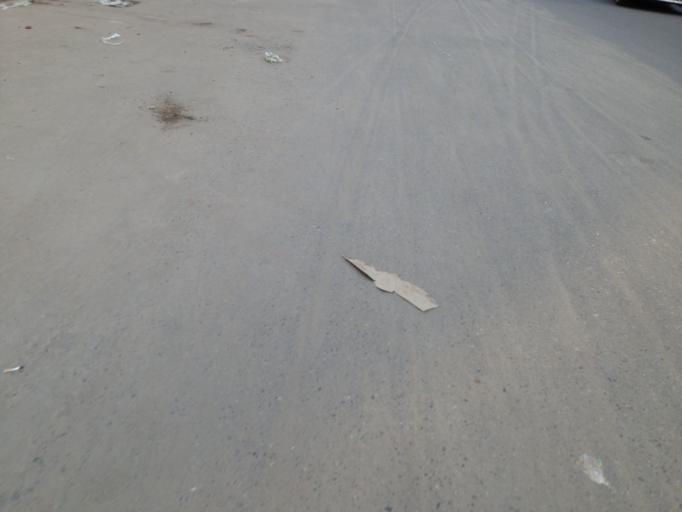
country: BD
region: Dhaka
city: Tungi
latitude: 23.8742
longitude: 90.3830
